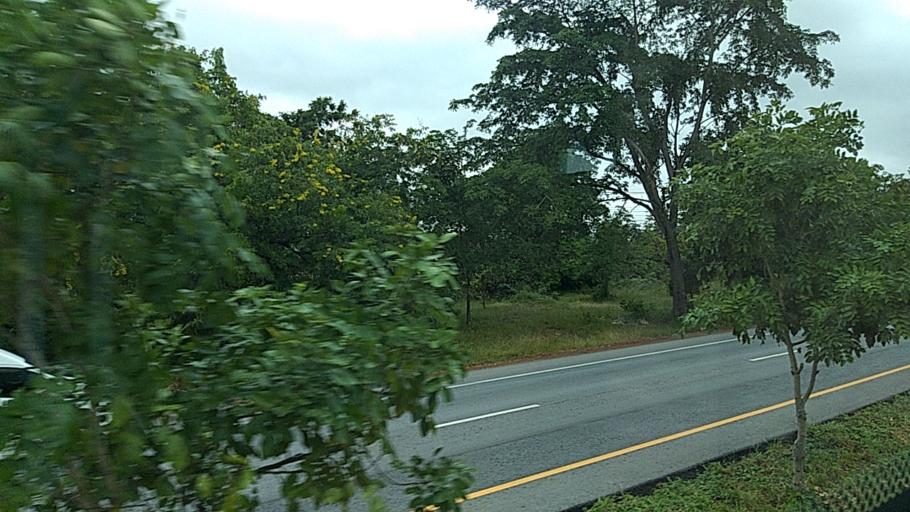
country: TH
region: Khon Kaen
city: Phon
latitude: 15.7240
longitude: 102.5929
